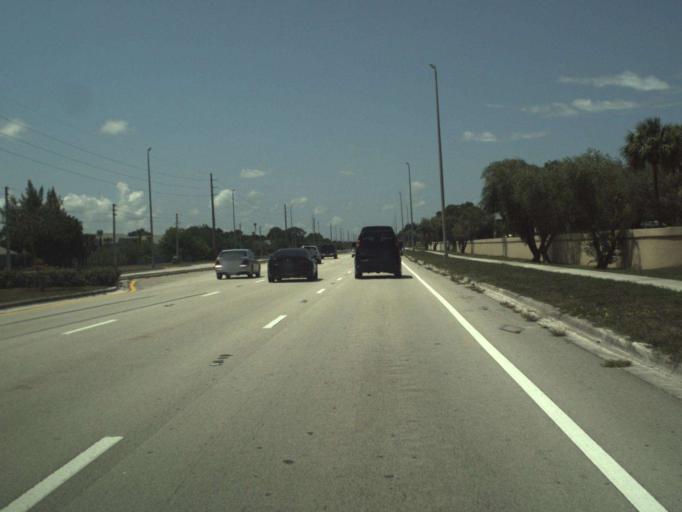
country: US
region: Florida
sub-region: Saint Lucie County
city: Port Saint Lucie
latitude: 27.2890
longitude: -80.2986
